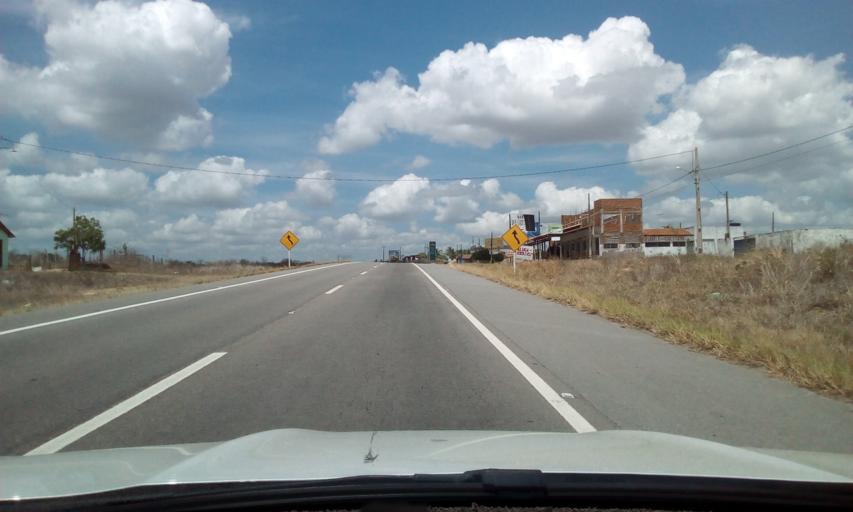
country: BR
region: Paraiba
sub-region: Gurinhem
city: Gurinhem
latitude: -7.1690
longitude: -35.3326
